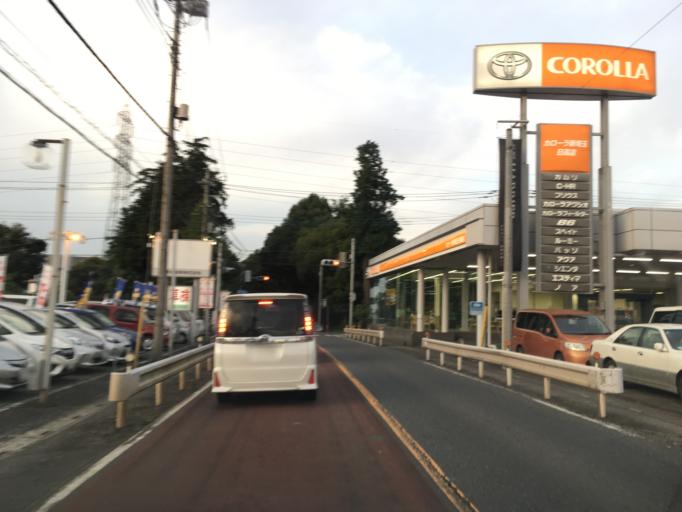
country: JP
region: Saitama
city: Sayama
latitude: 35.8877
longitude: 139.3784
